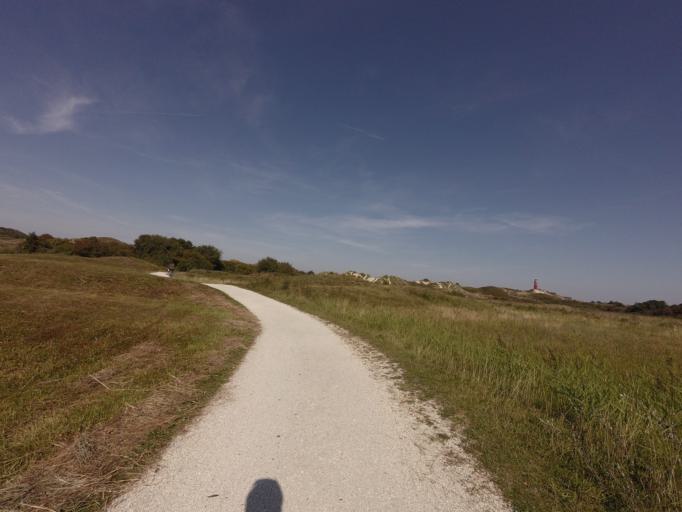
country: NL
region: Friesland
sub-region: Gemeente Schiermonnikoog
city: Schiermonnikoog
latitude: 53.4817
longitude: 6.1467
